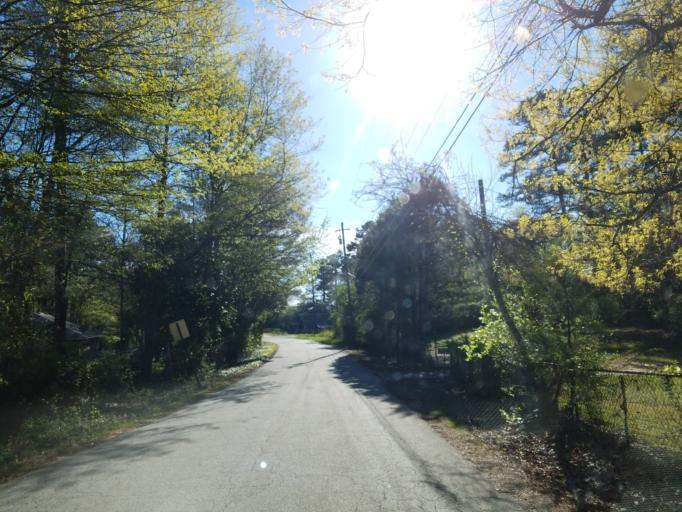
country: US
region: Georgia
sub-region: Cobb County
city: Marietta
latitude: 33.9608
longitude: -84.5106
